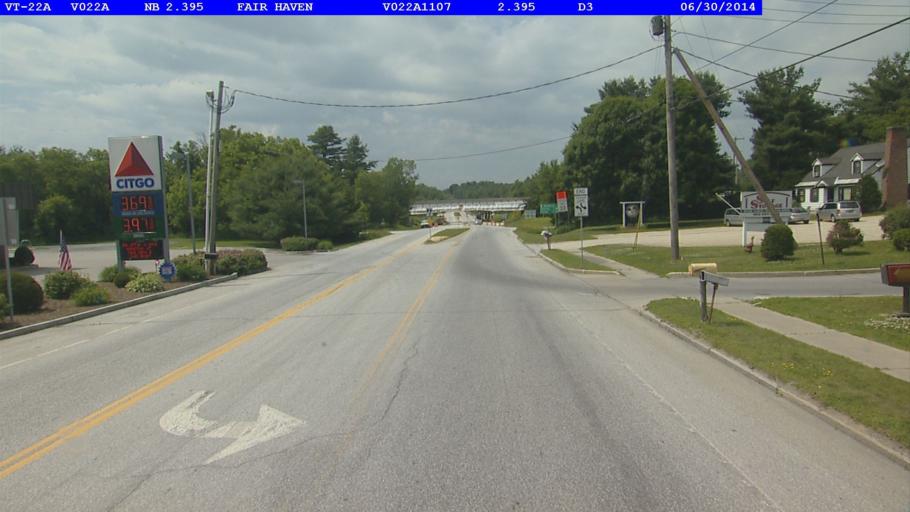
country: US
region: Vermont
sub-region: Rutland County
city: Fair Haven
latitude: 43.6040
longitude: -73.2764
